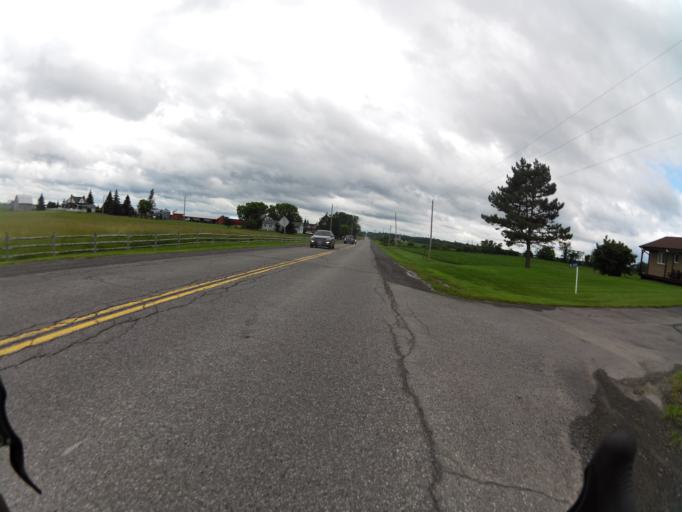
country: CA
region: Ontario
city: Bells Corners
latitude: 45.2544
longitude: -75.8757
